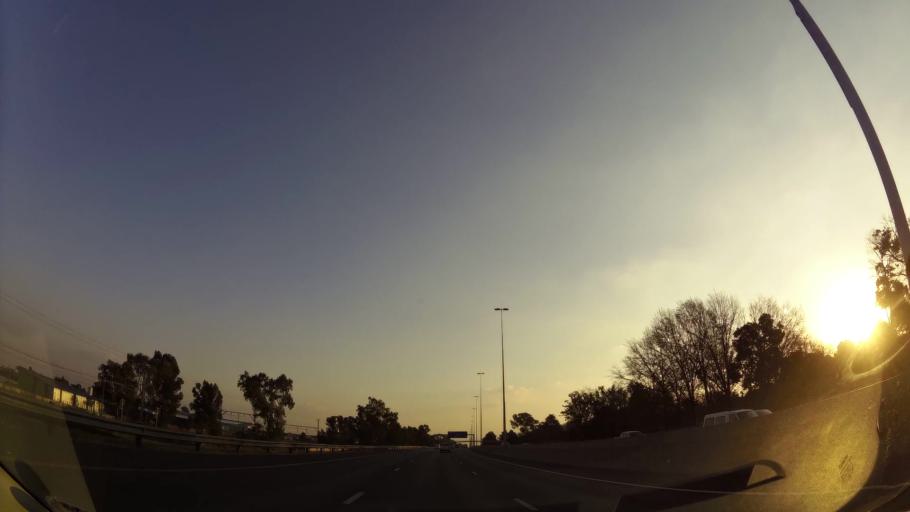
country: ZA
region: Gauteng
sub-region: Ekurhuleni Metropolitan Municipality
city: Benoni
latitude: -26.1711
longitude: 28.3480
